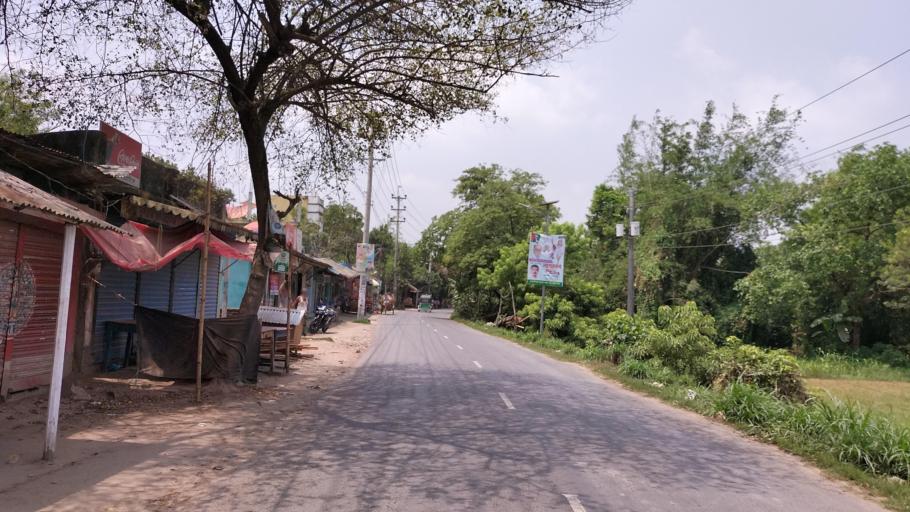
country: BD
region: Dhaka
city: Azimpur
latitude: 23.7297
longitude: 90.2859
